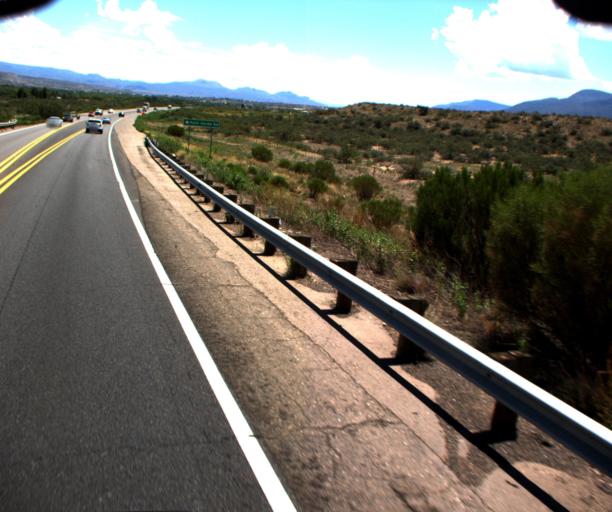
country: US
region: Arizona
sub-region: Yavapai County
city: Camp Verde
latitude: 34.5968
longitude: -111.8944
